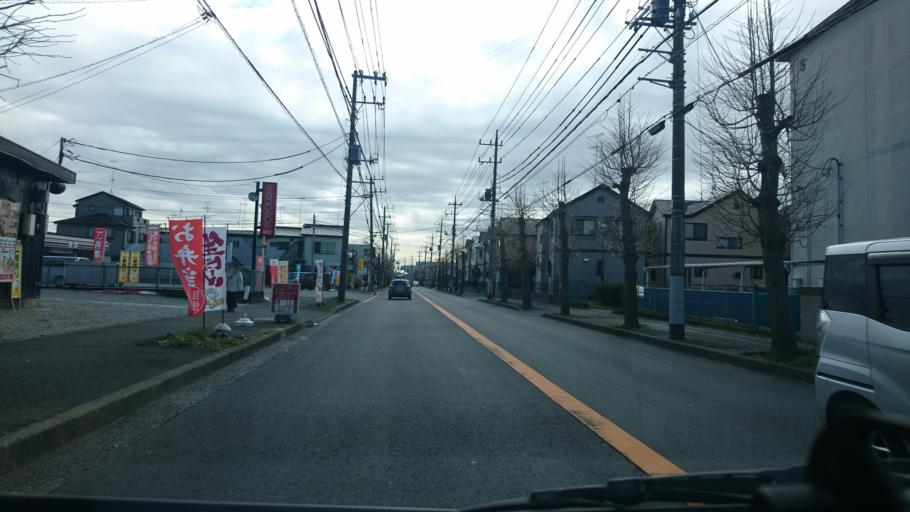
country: JP
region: Kanagawa
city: Zama
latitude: 35.5259
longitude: 139.3345
